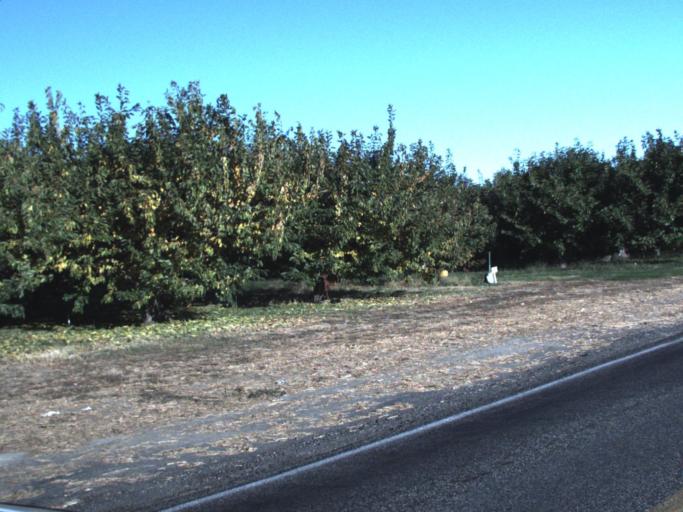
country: US
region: Washington
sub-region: Benton County
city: Benton City
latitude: 46.2840
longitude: -119.4941
